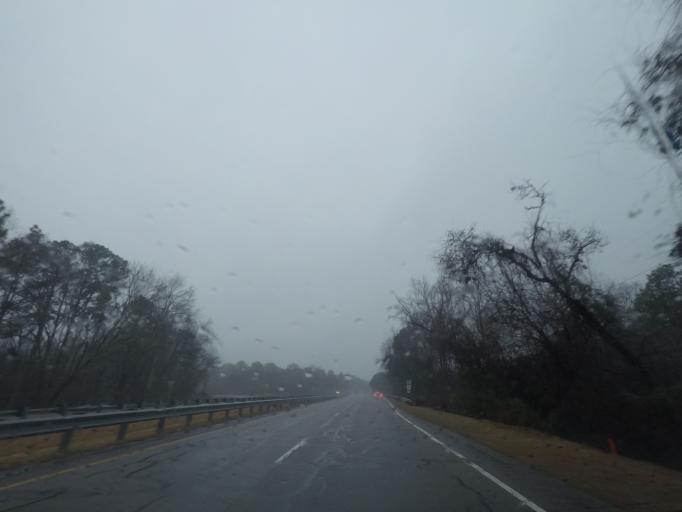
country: US
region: North Carolina
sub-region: Moore County
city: Southern Pines
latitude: 35.1931
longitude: -79.3817
